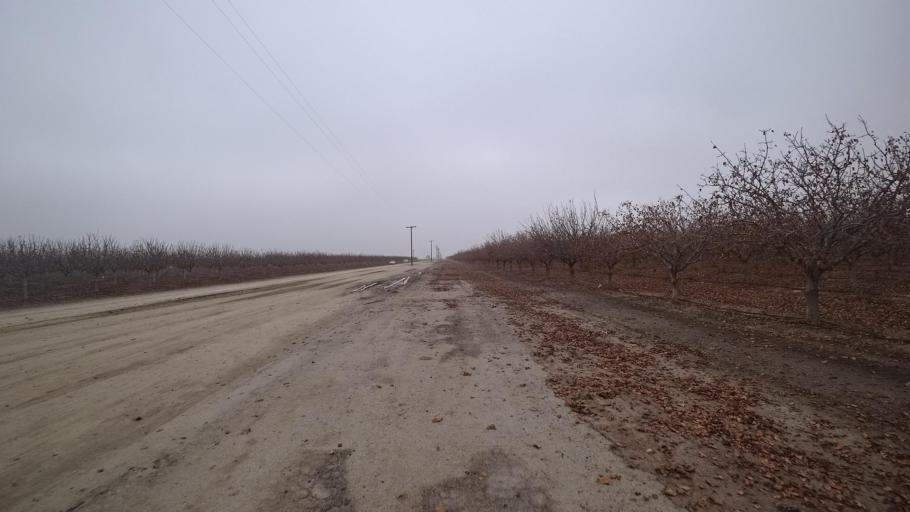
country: US
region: California
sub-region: Kern County
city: Wasco
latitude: 35.6854
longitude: -119.4907
